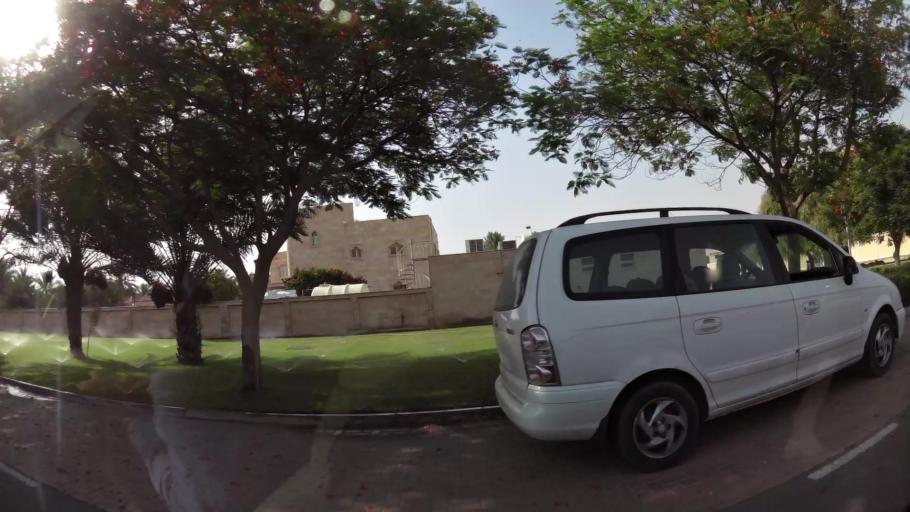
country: AE
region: Ash Shariqah
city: Sharjah
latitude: 25.2491
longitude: 55.4228
